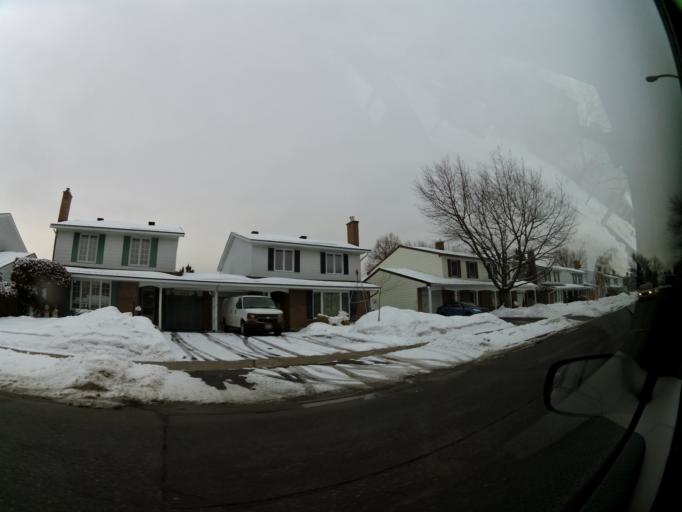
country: CA
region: Quebec
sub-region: Outaouais
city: Gatineau
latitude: 45.4545
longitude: -75.5945
